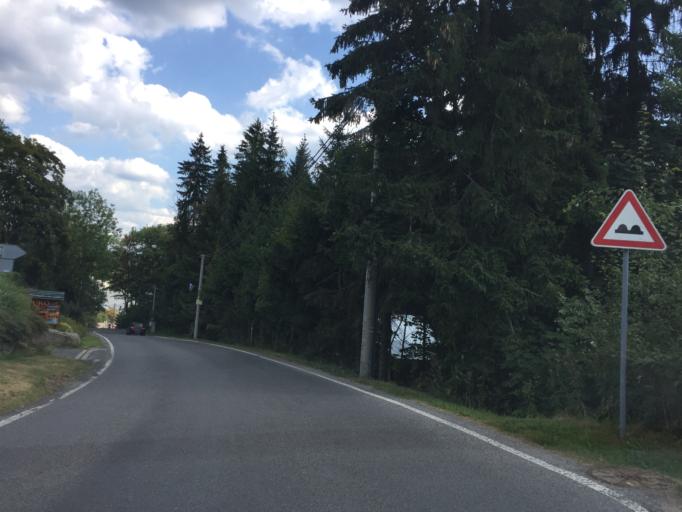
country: CZ
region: Liberecky
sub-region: Okres Jablonec nad Nisou
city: Janov nad Nisou
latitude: 50.7868
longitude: 15.1518
